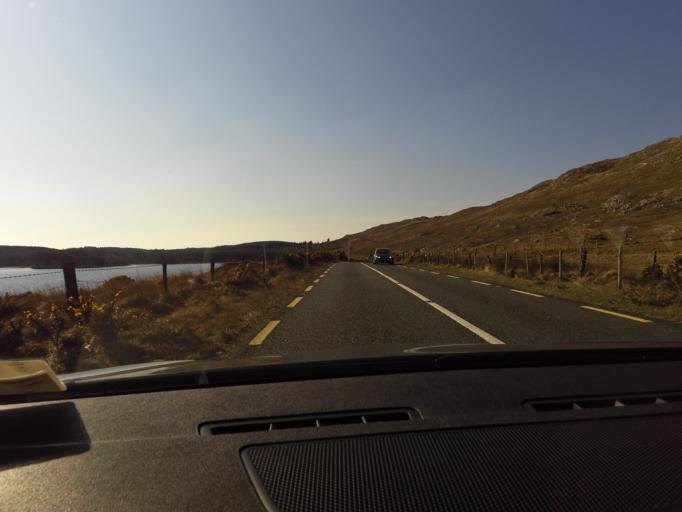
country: IE
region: Connaught
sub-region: County Galway
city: Clifden
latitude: 53.4707
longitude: -9.8567
